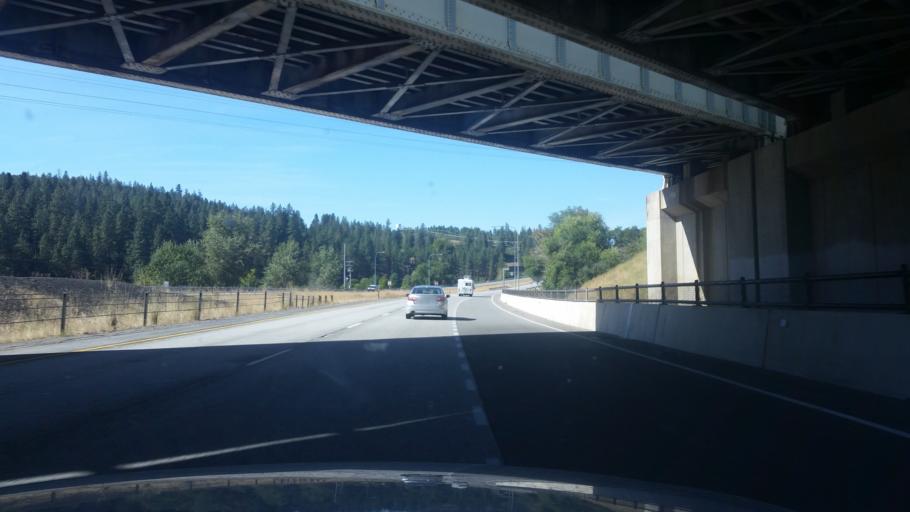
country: US
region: Washington
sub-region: Spokane County
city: Spokane
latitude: 47.6225
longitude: -117.4370
